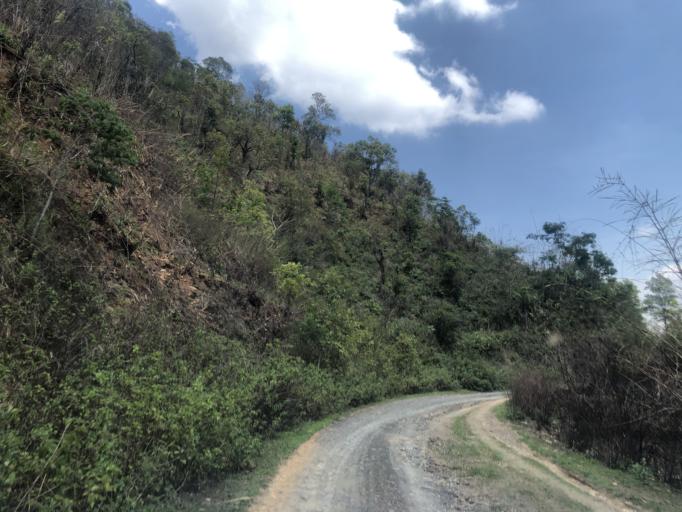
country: LA
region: Phongsali
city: Phongsali
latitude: 21.4348
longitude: 102.1615
